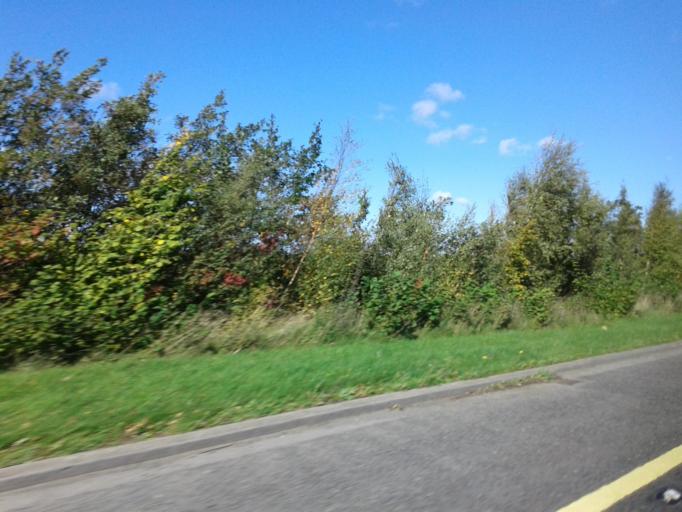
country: IE
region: Leinster
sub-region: Fingal County
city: Blanchardstown
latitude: 53.4519
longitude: -6.3550
